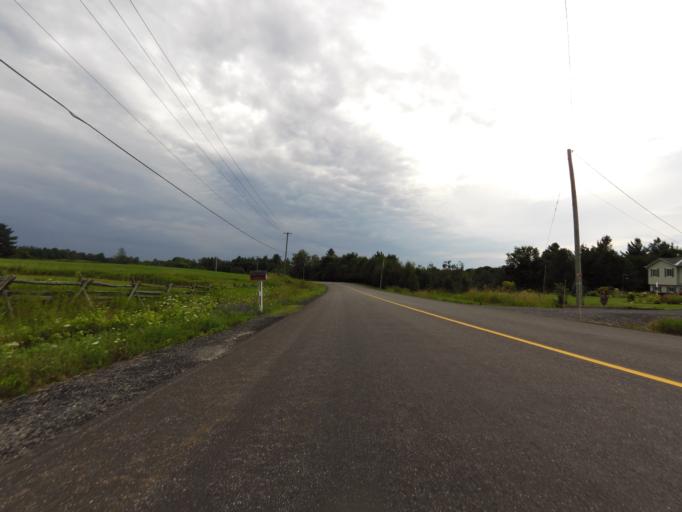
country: CA
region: Ontario
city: Perth
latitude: 45.0921
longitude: -76.3979
